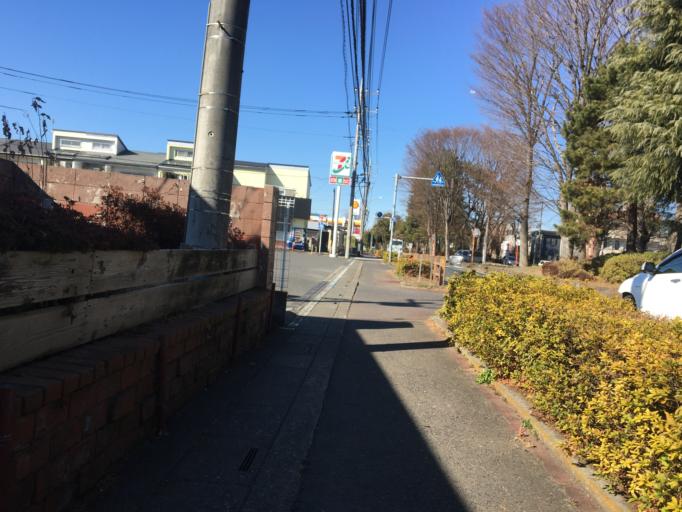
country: JP
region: Saitama
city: Oi
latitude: 35.8415
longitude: 139.5236
